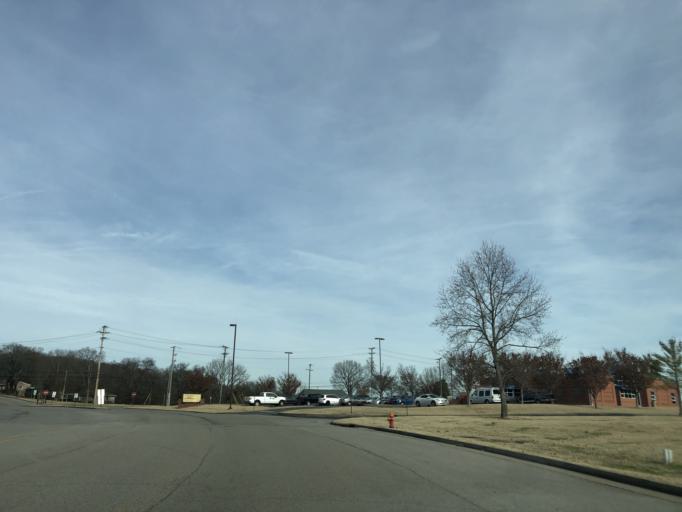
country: US
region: Tennessee
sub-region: Davidson County
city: Nashville
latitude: 36.2162
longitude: -86.7439
